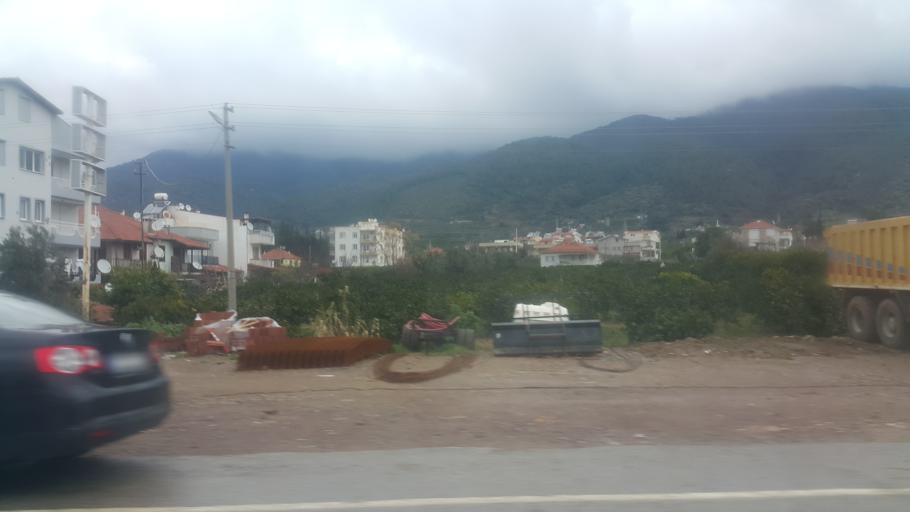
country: TR
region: Izmir
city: Ozdere
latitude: 38.0464
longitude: 27.0570
